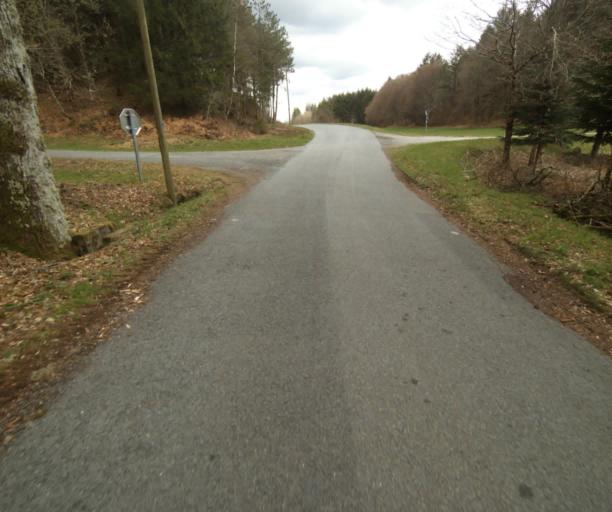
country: FR
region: Limousin
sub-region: Departement de la Correze
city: Correze
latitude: 45.3235
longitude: 1.9544
